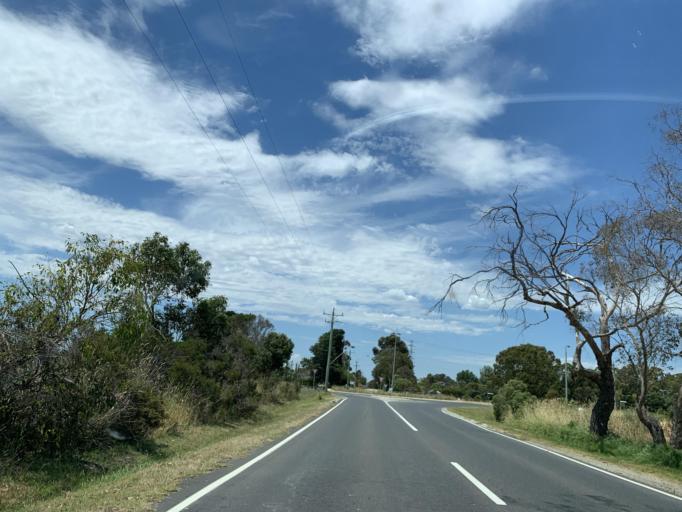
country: AU
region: Victoria
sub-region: Mornington Peninsula
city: Tyabb
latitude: -38.2387
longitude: 145.2324
